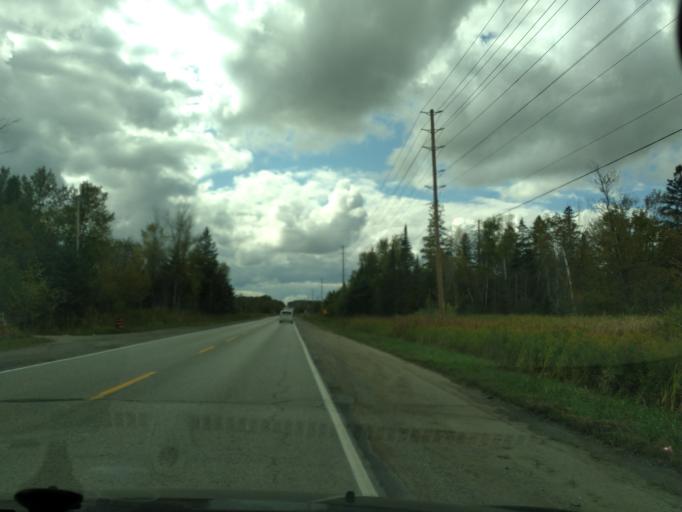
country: CA
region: Ontario
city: Innisfil
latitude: 44.2960
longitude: -79.6312
